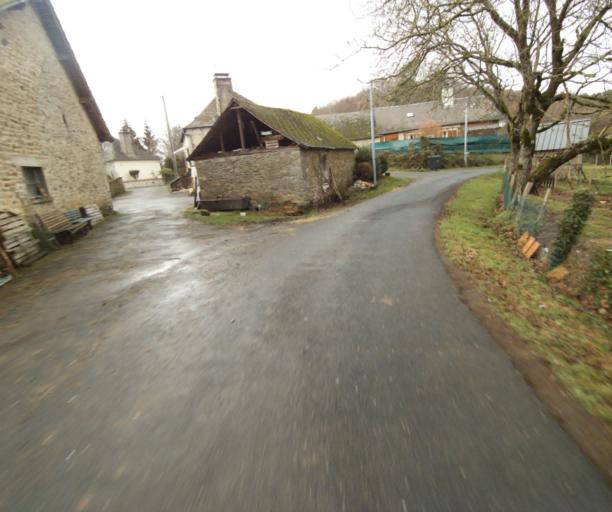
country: FR
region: Limousin
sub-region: Departement de la Correze
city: Saint-Mexant
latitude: 45.2967
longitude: 1.6319
